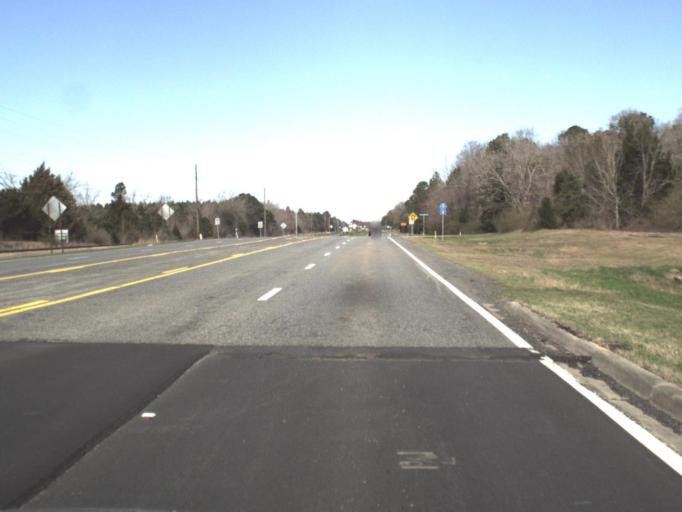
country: US
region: Florida
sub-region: Washington County
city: Chipley
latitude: 30.7042
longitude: -85.3915
